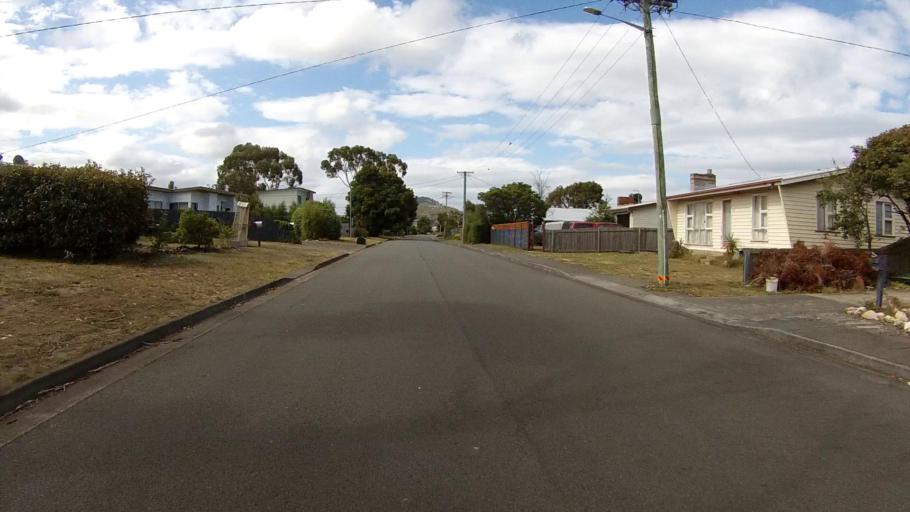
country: AU
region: Tasmania
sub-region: Clarence
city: Lauderdale
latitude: -42.9038
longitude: 147.4924
